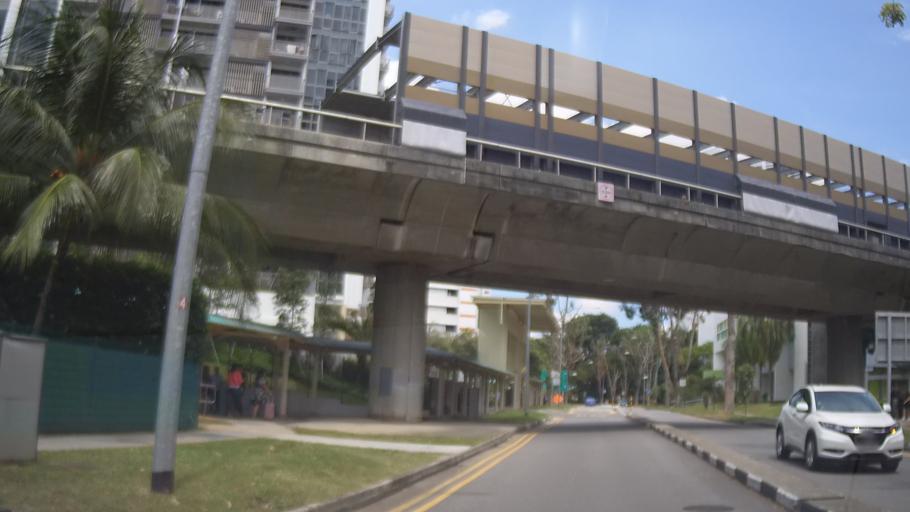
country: SG
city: Singapore
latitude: 1.3164
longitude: 103.8851
